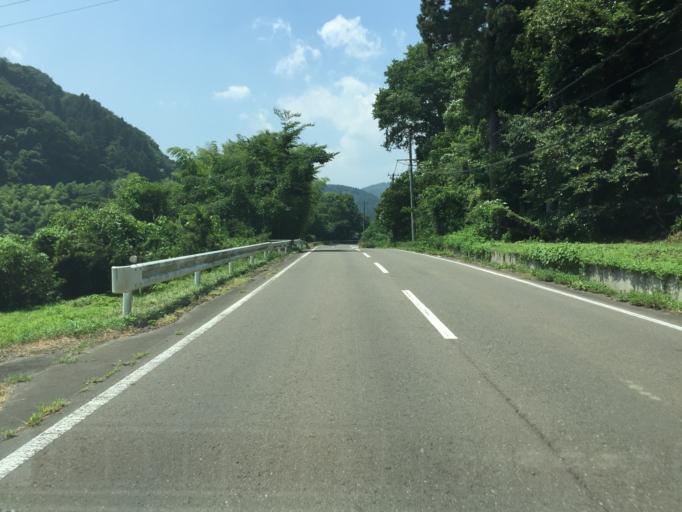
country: JP
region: Miyagi
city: Marumori
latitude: 37.9347
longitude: 140.7140
